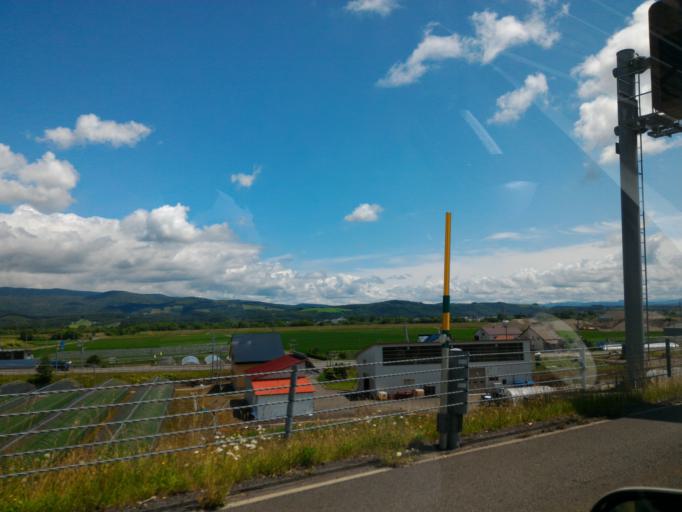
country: JP
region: Hokkaido
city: Nayoro
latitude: 44.3706
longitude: 142.4342
